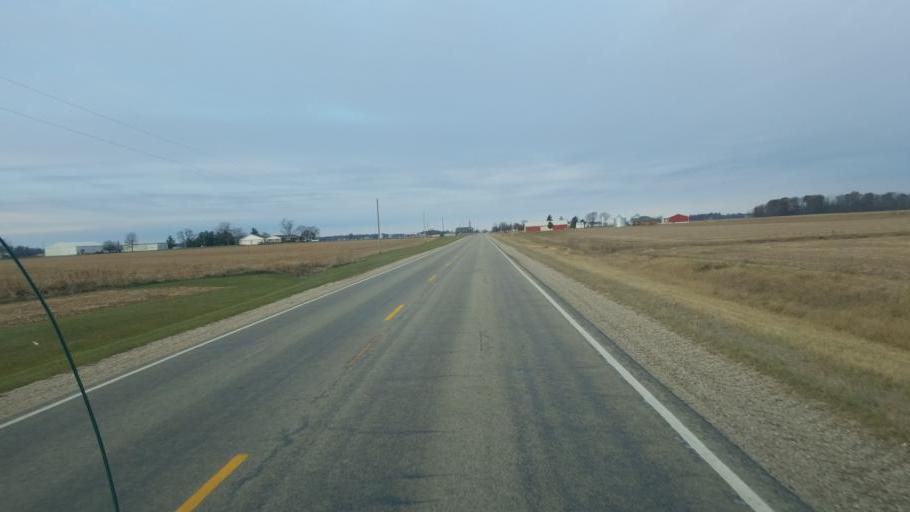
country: US
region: Ohio
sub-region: Mercer County
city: Fort Recovery
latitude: 40.5426
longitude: -84.8216
